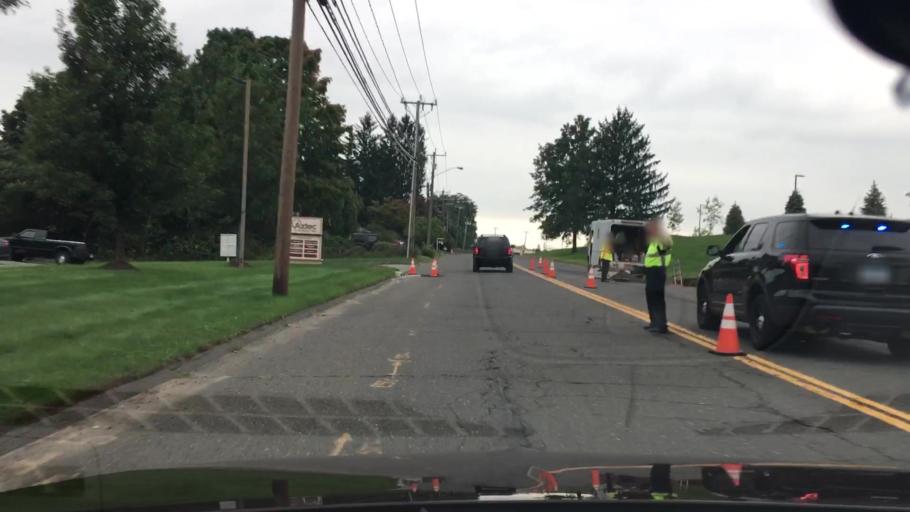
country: US
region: Connecticut
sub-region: Hartford County
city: Kensington
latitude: 41.5966
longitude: -72.7214
